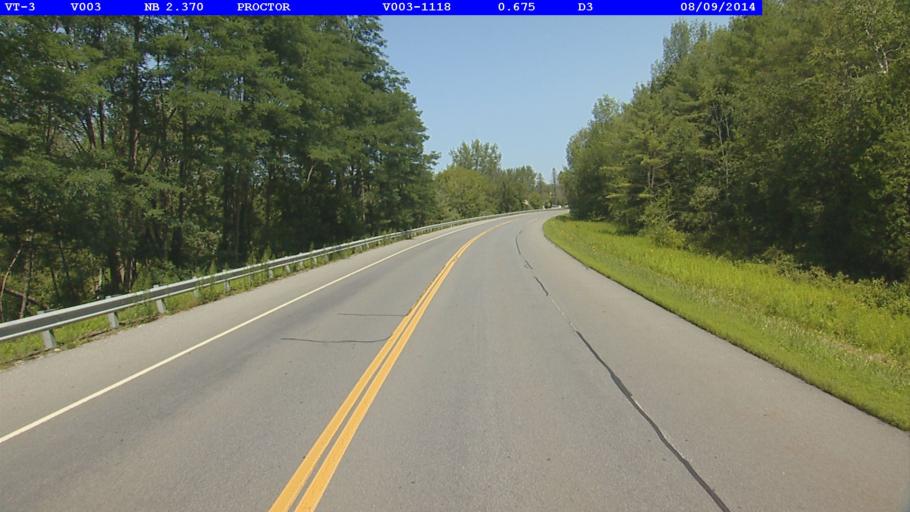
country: US
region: Vermont
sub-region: Rutland County
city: West Rutland
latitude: 43.6338
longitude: -73.0349
